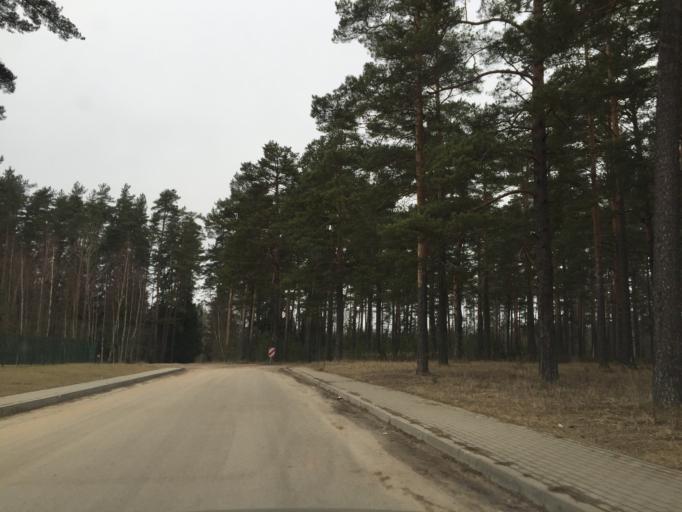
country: LV
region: Garkalne
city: Garkalne
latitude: 56.9655
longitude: 24.4262
